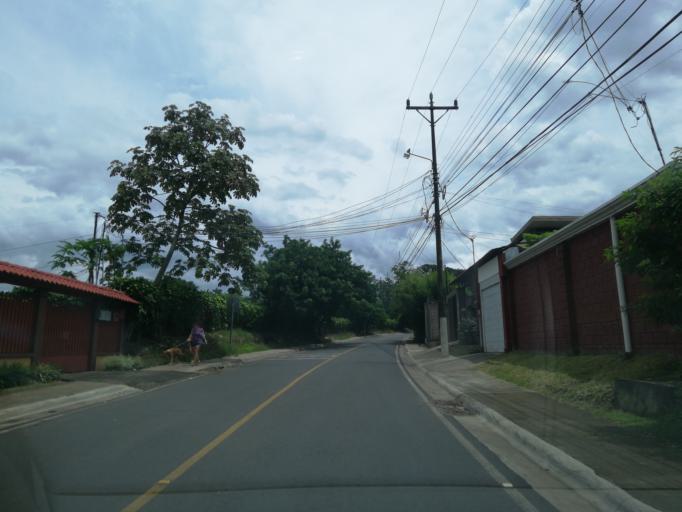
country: CR
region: Alajuela
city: Alajuela
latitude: 10.0216
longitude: -84.1974
